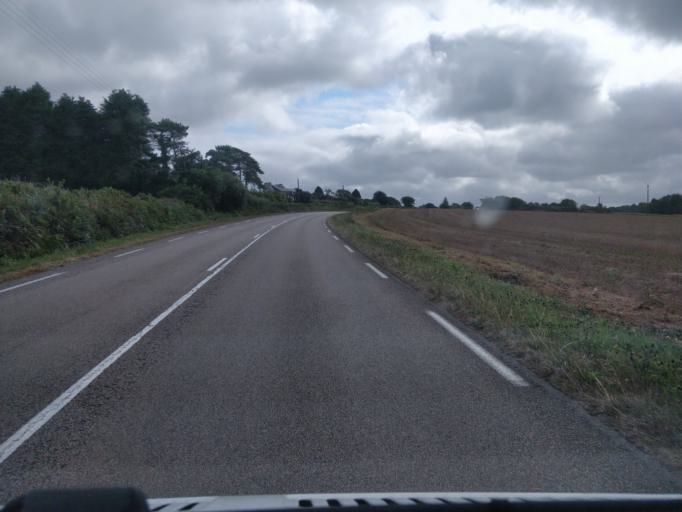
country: FR
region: Brittany
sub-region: Departement du Finistere
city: Plogastel-Saint-Germain
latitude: 47.9986
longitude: -4.2624
